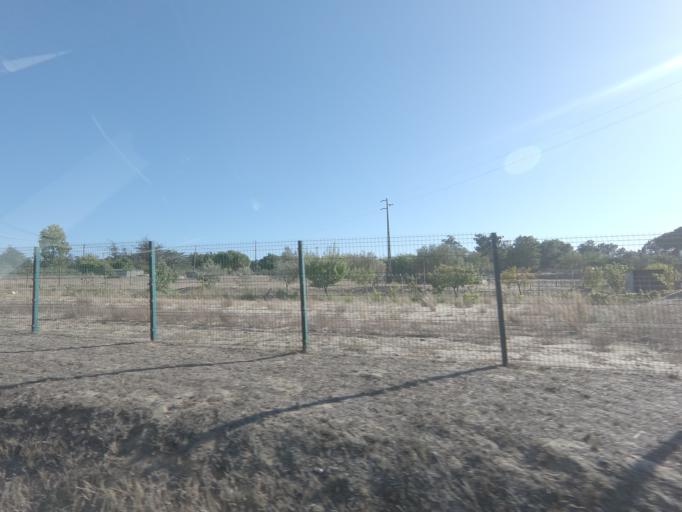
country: PT
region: Setubal
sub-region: Palmela
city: Pinhal Novo
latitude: 38.6112
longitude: -8.9470
